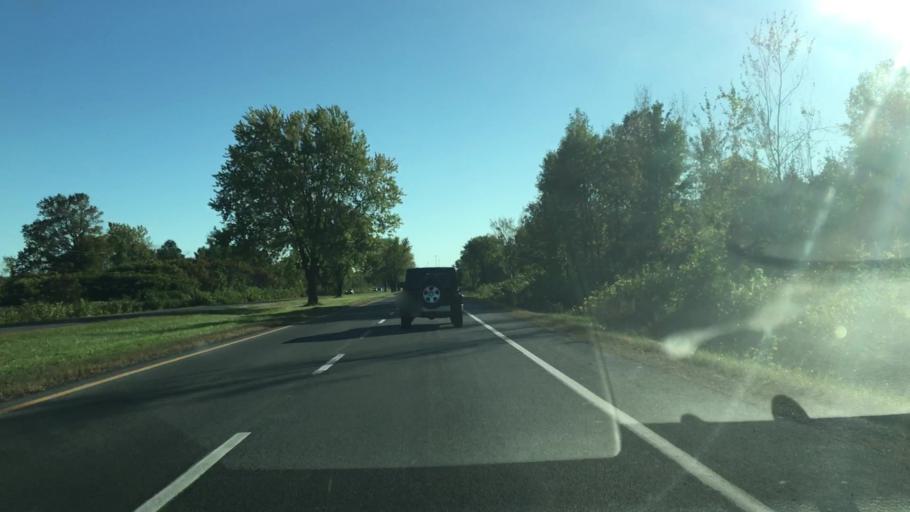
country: CA
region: Quebec
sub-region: Monteregie
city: Les Coteaux
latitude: 45.2864
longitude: -74.1880
